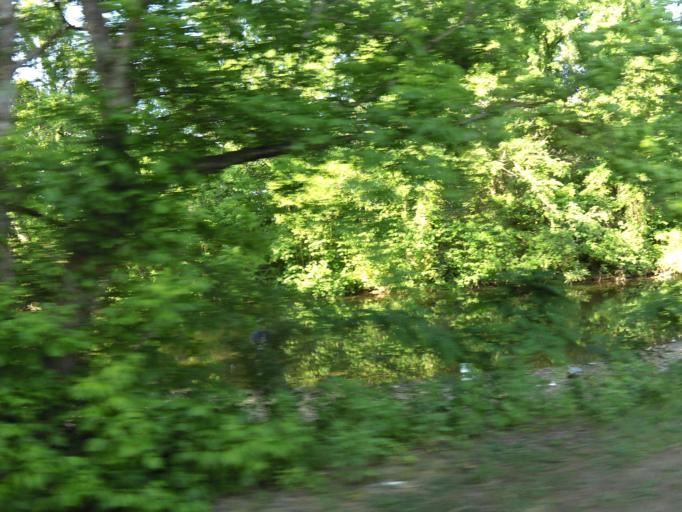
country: US
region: Tennessee
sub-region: Sevier County
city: Pigeon Forge
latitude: 35.8176
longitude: -83.5907
